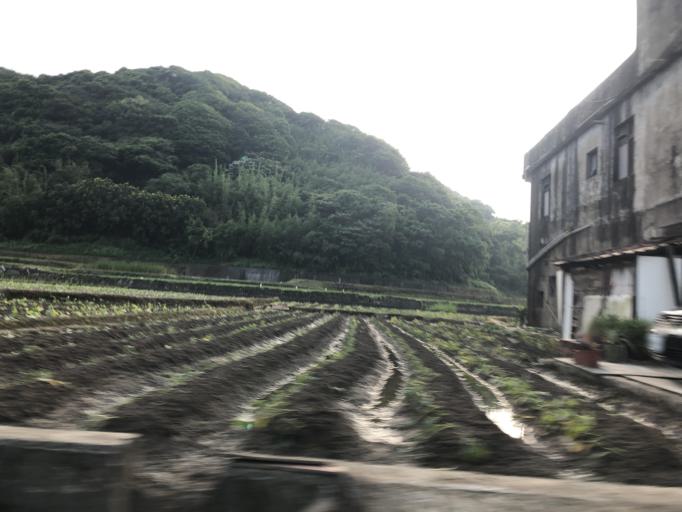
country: TW
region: Taiwan
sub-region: Keelung
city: Keelung
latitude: 25.2085
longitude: 121.6470
